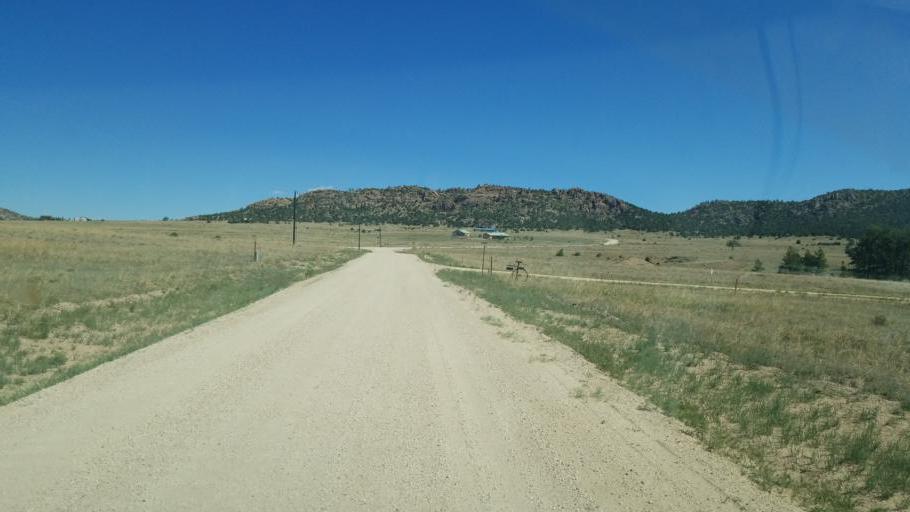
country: US
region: Colorado
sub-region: Custer County
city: Westcliffe
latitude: 38.2240
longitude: -105.4580
